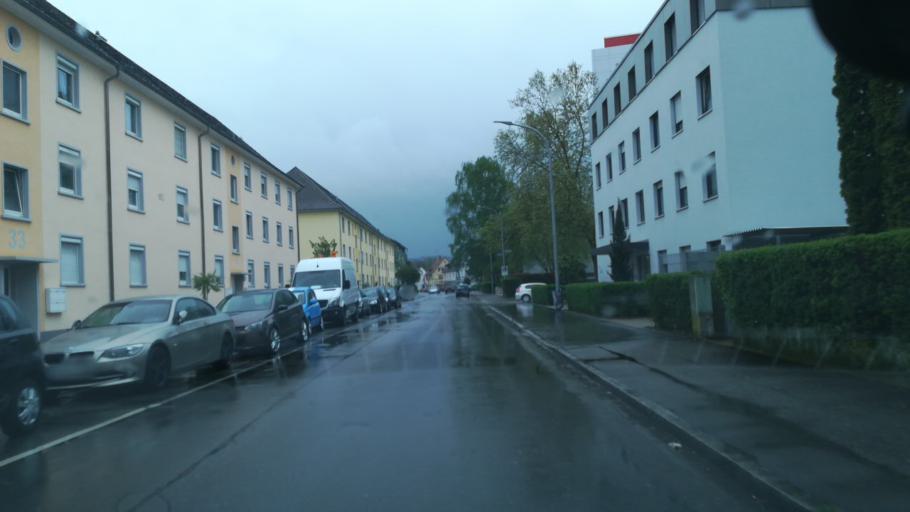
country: DE
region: Baden-Wuerttemberg
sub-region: Freiburg Region
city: Singen
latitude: 47.7487
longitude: 8.8450
